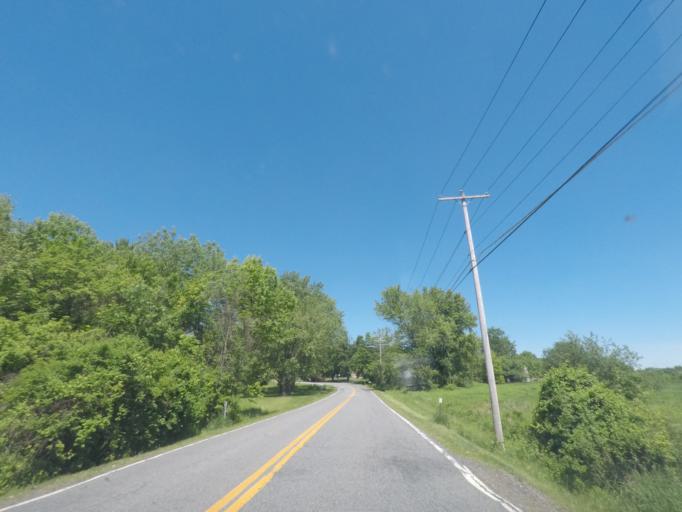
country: US
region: New York
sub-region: Saratoga County
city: Country Knolls
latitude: 42.8722
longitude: -73.8533
